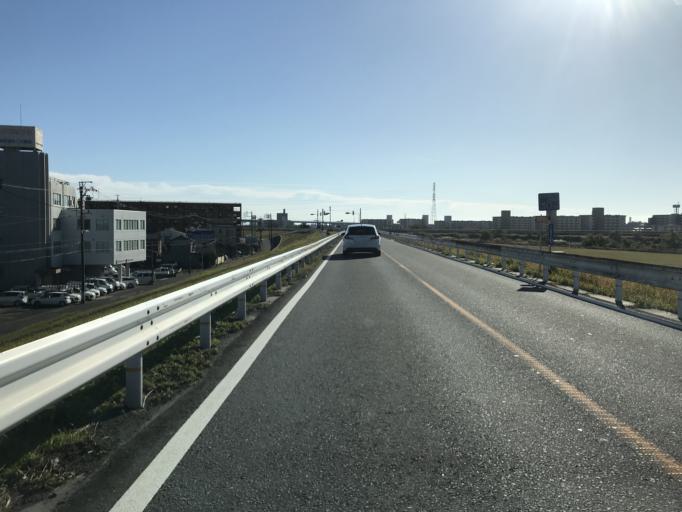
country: JP
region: Aichi
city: Kanie
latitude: 35.1666
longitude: 136.8360
